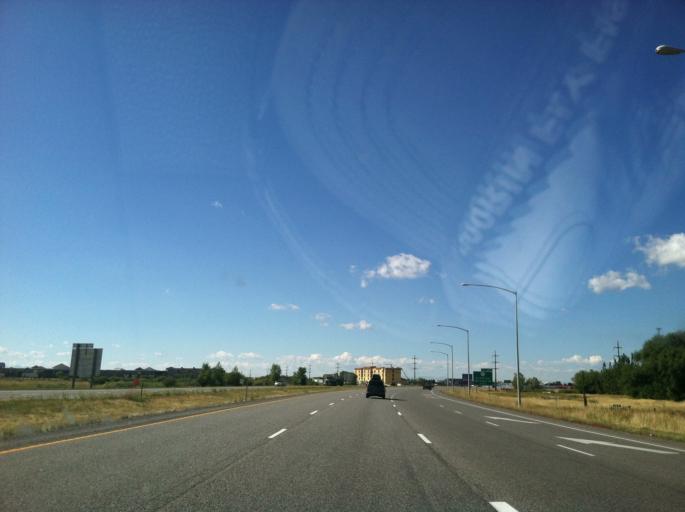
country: US
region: Montana
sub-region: Gallatin County
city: Bozeman
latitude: 45.6988
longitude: -111.0527
